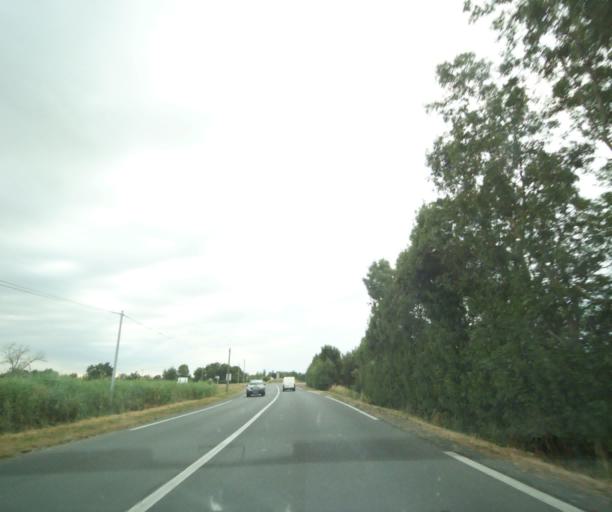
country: FR
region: Pays de la Loire
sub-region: Departement de la Vendee
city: Chaille-les-Marais
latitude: 46.4075
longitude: -1.0361
